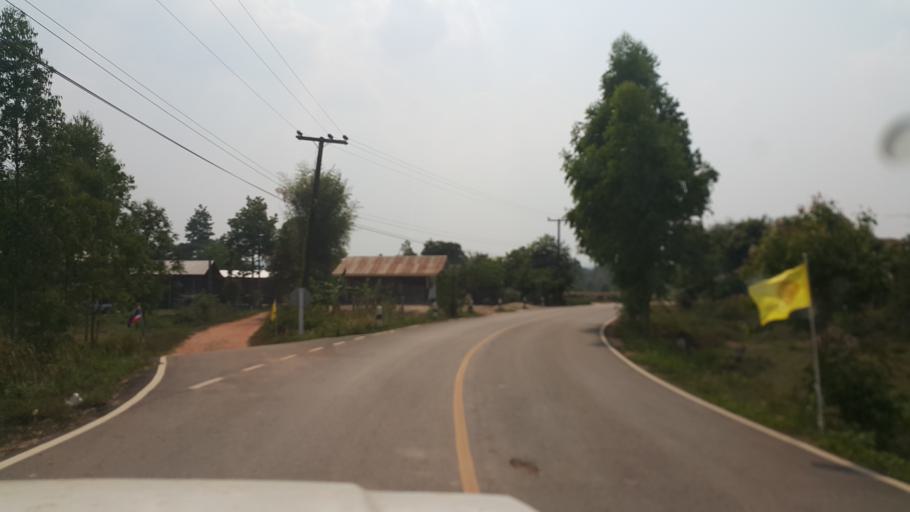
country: TH
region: Nakhon Phanom
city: Ban Phaeng
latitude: 17.9598
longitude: 104.1862
